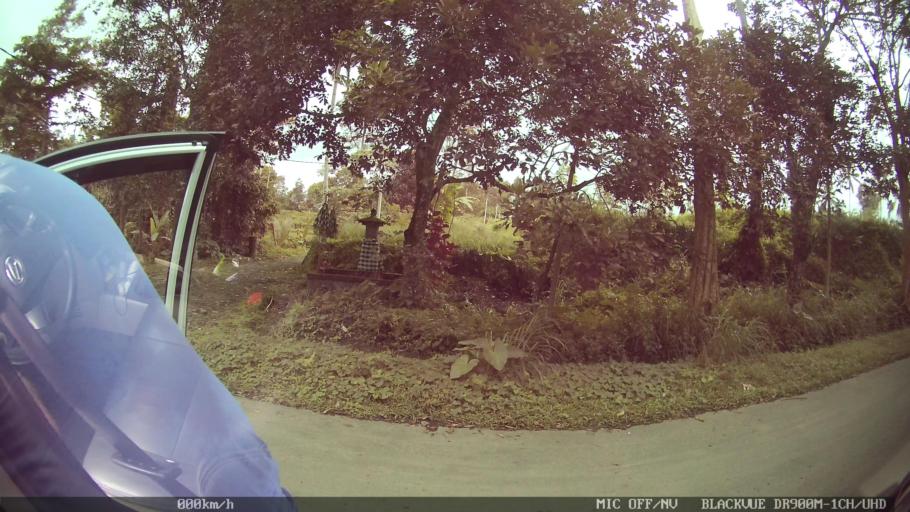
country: ID
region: Bali
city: Peneng
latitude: -8.3573
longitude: 115.2054
